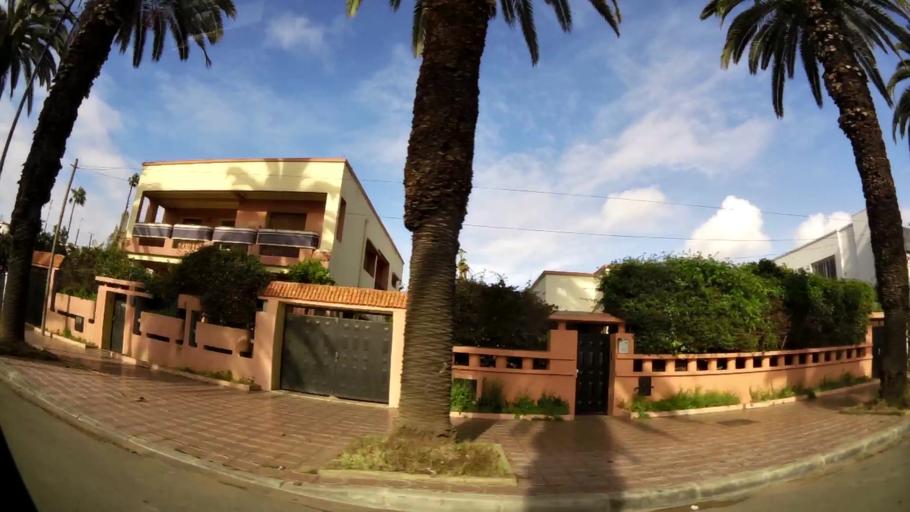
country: MA
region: Grand Casablanca
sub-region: Mohammedia
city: Mohammedia
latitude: 33.6998
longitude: -7.3931
